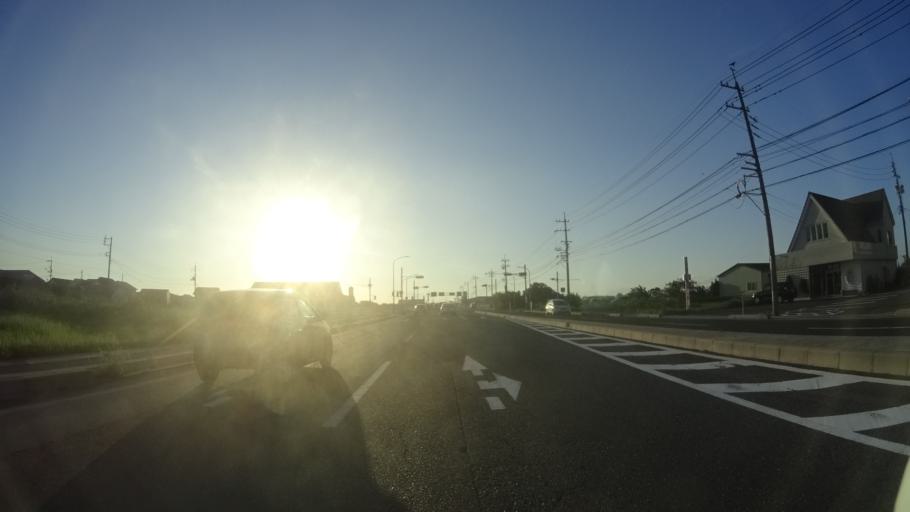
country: JP
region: Tottori
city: Yonago
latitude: 35.4460
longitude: 133.3804
